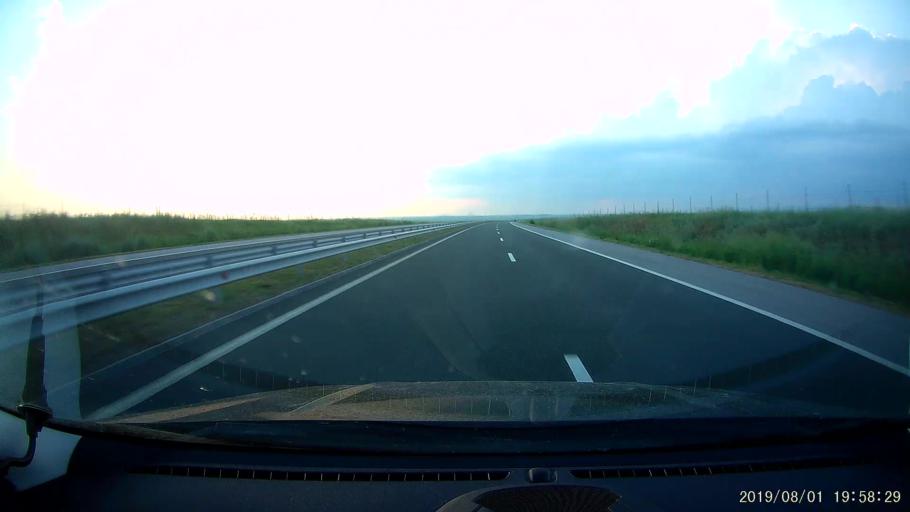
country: BG
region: Yambol
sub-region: Obshtina Straldzha
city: Straldzha
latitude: 42.5450
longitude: 26.7635
